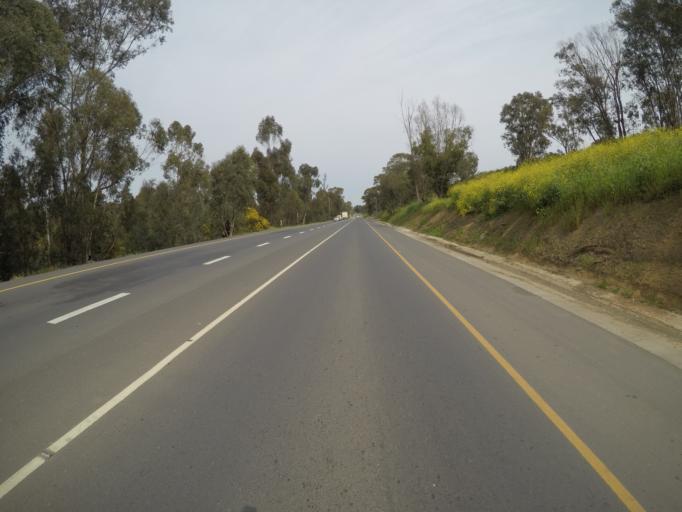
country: ZA
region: Western Cape
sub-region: West Coast District Municipality
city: Malmesbury
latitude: -33.4616
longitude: 18.7433
